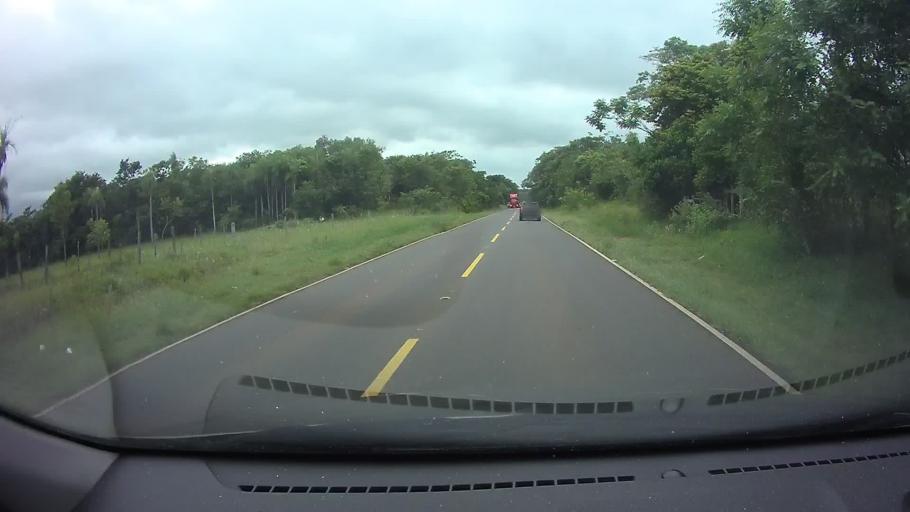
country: PY
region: Paraguari
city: Carapegua
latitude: -25.7307
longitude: -57.3085
